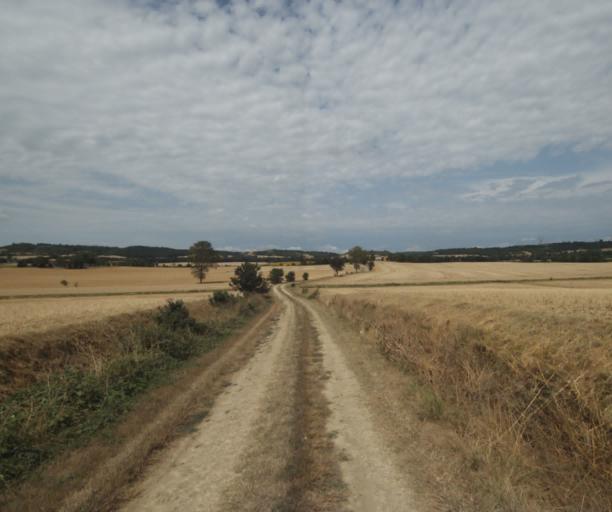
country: FR
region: Midi-Pyrenees
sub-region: Departement de la Haute-Garonne
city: Saint-Felix-Lauragais
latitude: 43.4140
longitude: 1.8986
